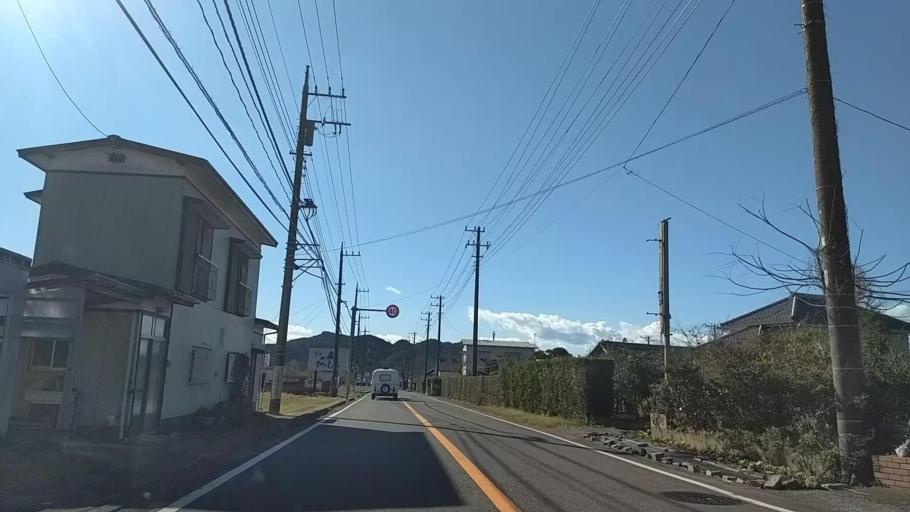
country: JP
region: Chiba
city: Tateyama
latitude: 34.9353
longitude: 139.8402
